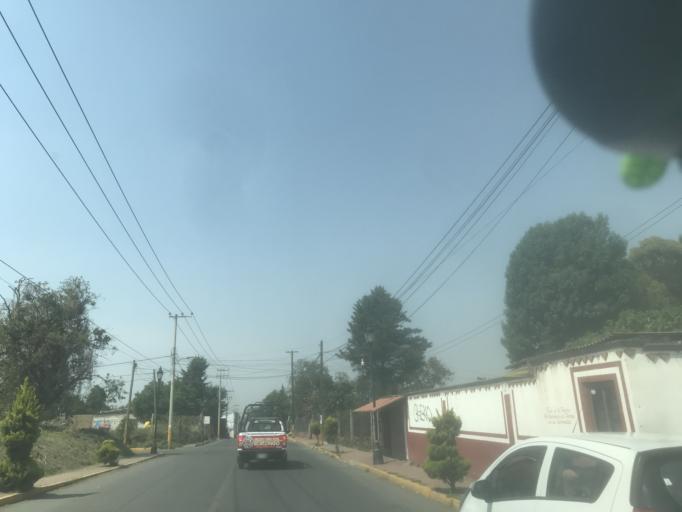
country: MX
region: Mexico
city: Ozumba de Alzate
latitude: 19.0316
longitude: -98.7998
